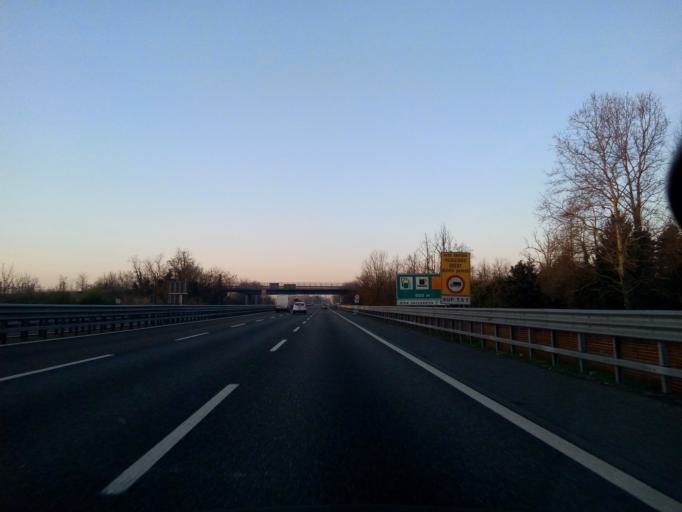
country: IT
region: Lombardy
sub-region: Citta metropolitana di Milano
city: Cesano Boscone
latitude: 45.4515
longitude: 9.0759
